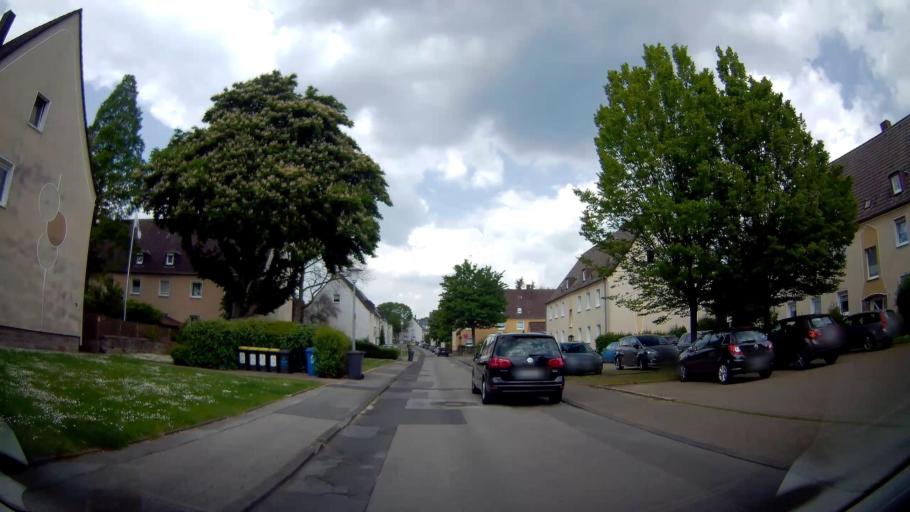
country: DE
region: North Rhine-Westphalia
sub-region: Regierungsbezirk Munster
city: Gladbeck
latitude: 51.5444
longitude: 7.0261
